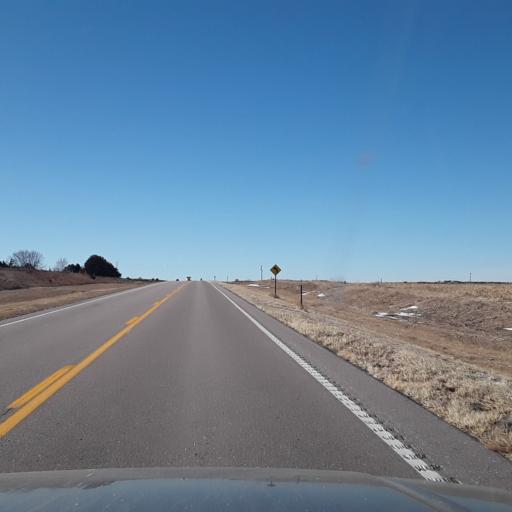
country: US
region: Nebraska
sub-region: Frontier County
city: Stockville
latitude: 40.7003
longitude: -100.2763
